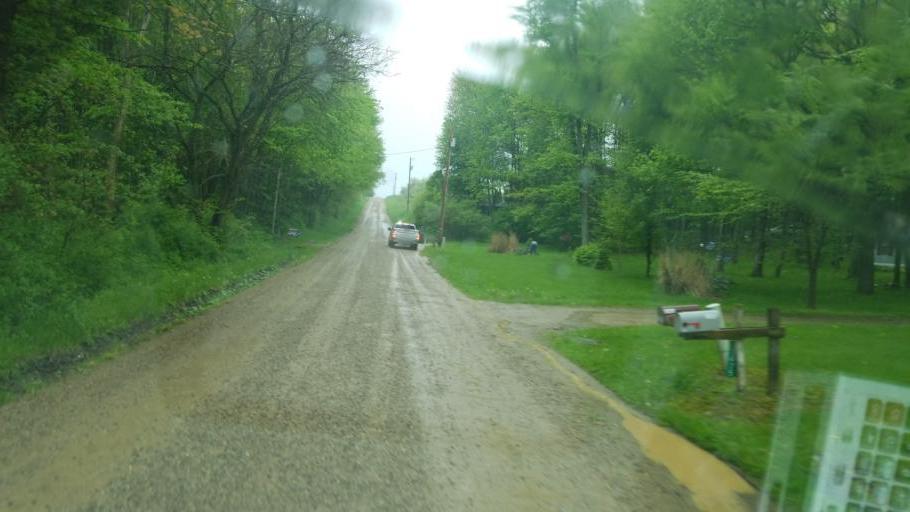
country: US
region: Ohio
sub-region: Knox County
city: Mount Vernon
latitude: 40.4649
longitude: -82.4338
